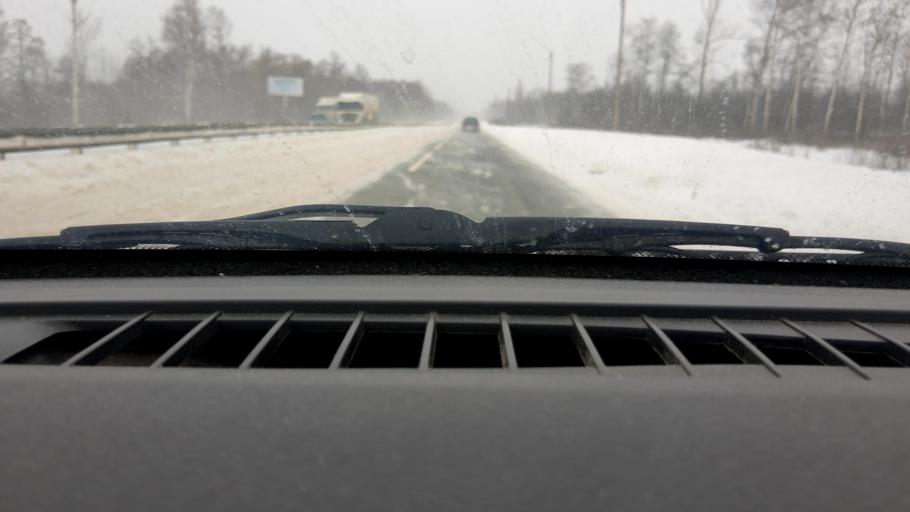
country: RU
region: Vladimir
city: Petushki
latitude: 55.9350
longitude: 39.4238
